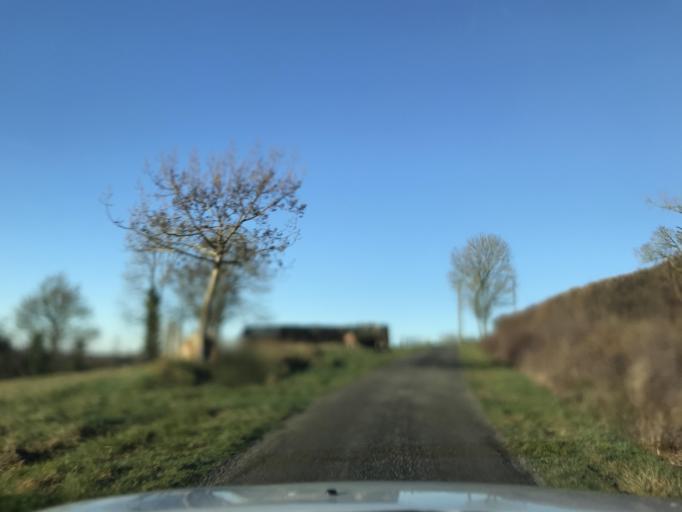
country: FR
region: Poitou-Charentes
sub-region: Departement de la Charente
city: Chasseneuil-sur-Bonnieure
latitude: 45.8388
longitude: 0.5045
